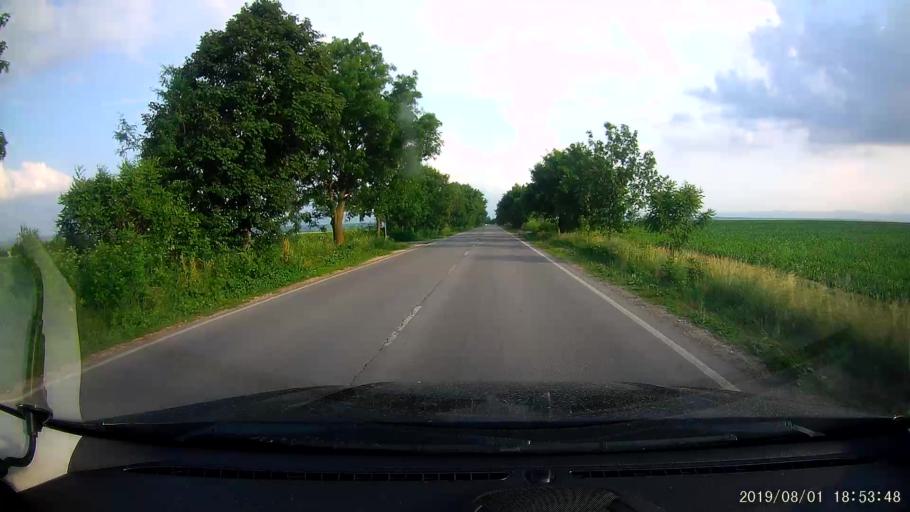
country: BG
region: Shumen
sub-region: Obshtina Shumen
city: Shumen
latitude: 43.2144
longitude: 26.9978
